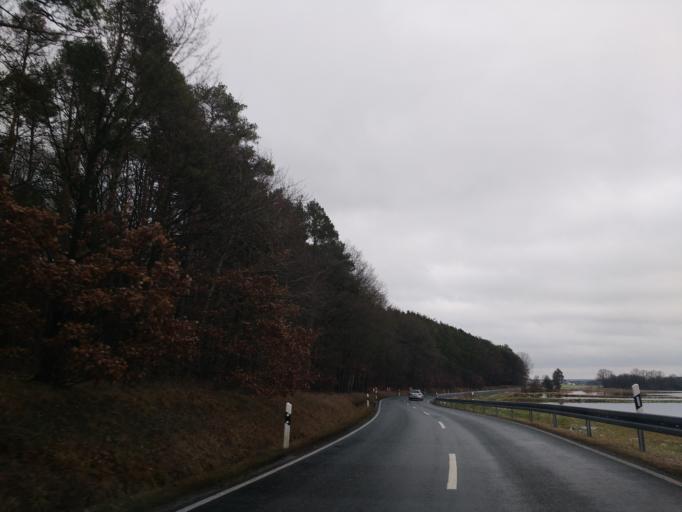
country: DE
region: Bavaria
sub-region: Regierungsbezirk Mittelfranken
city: Weisendorf
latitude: 49.6066
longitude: 10.8371
